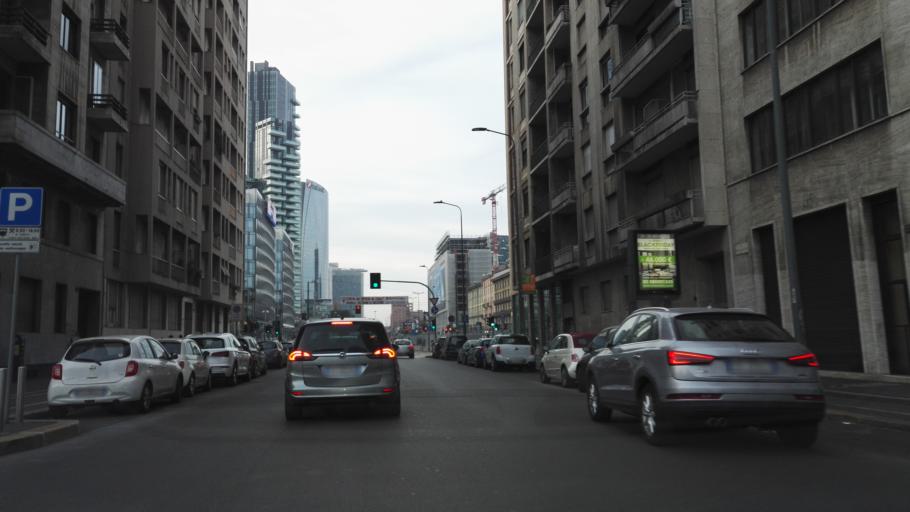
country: IT
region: Lombardy
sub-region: Citta metropolitana di Milano
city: Milano
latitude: 45.4806
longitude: 9.1984
